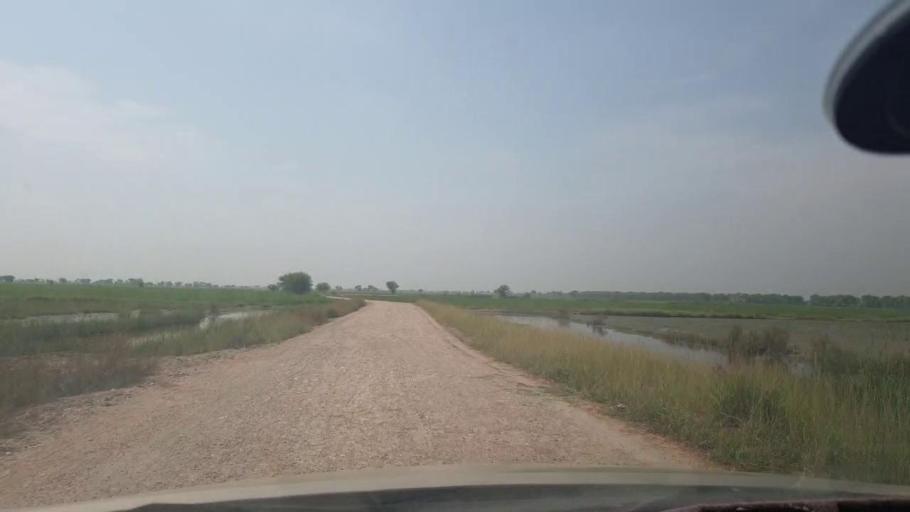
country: PK
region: Sindh
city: Jacobabad
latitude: 28.2669
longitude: 68.5112
